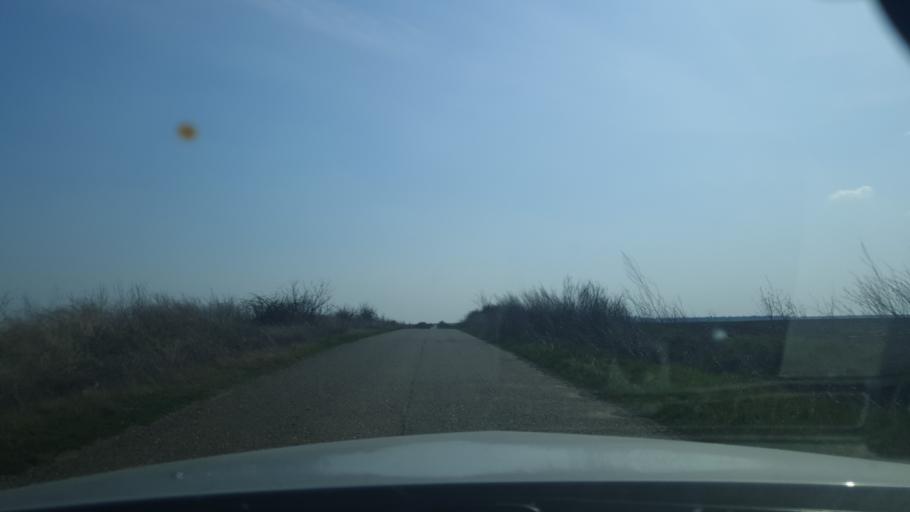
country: RS
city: Putinci
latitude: 45.0372
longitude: 19.9577
